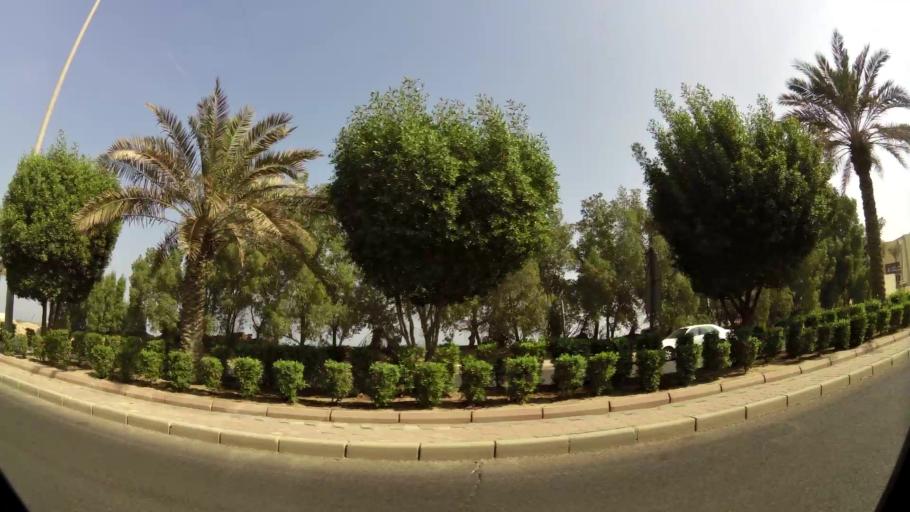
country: KW
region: Al Ahmadi
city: Al Manqaf
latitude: 29.1051
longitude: 48.1373
